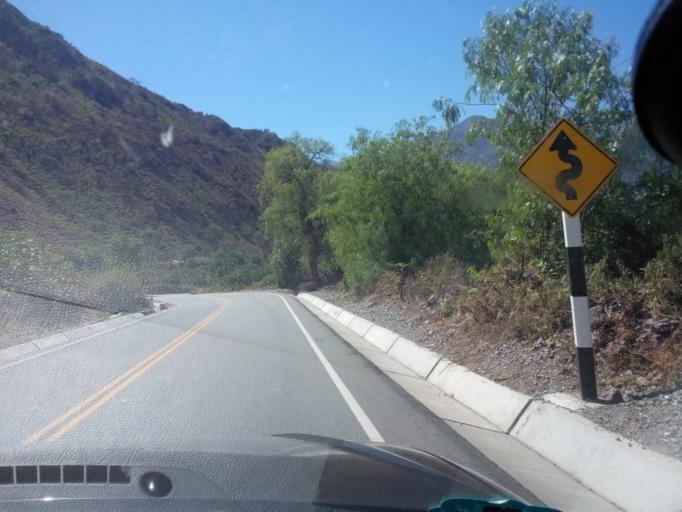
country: PE
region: Ayacucho
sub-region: Provincia de Huamanga
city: Ocros
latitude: -13.4229
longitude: -73.8631
